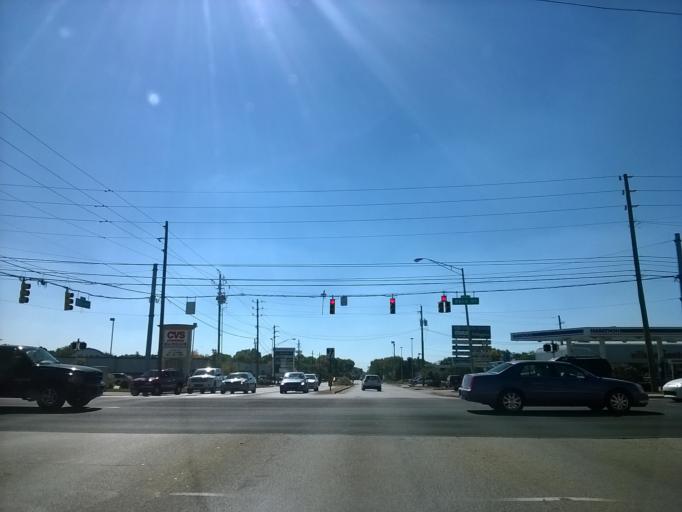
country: US
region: Indiana
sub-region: Marion County
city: Meridian Hills
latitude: 39.9124
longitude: -86.1840
